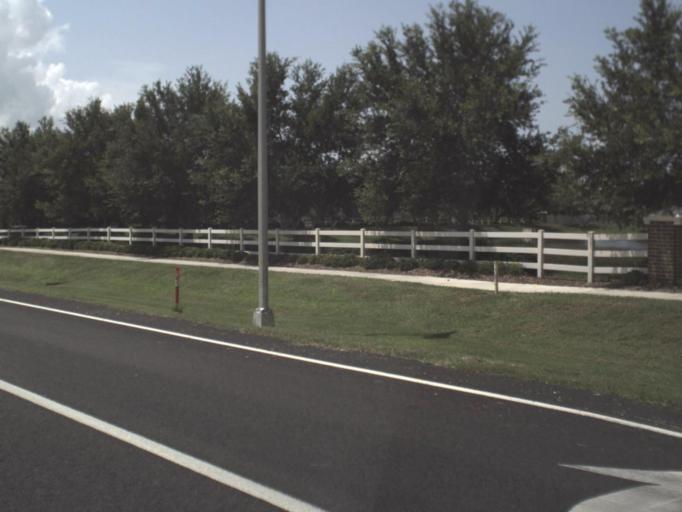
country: US
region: Florida
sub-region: Hillsborough County
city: Riverview
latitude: 27.8066
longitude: -82.3340
